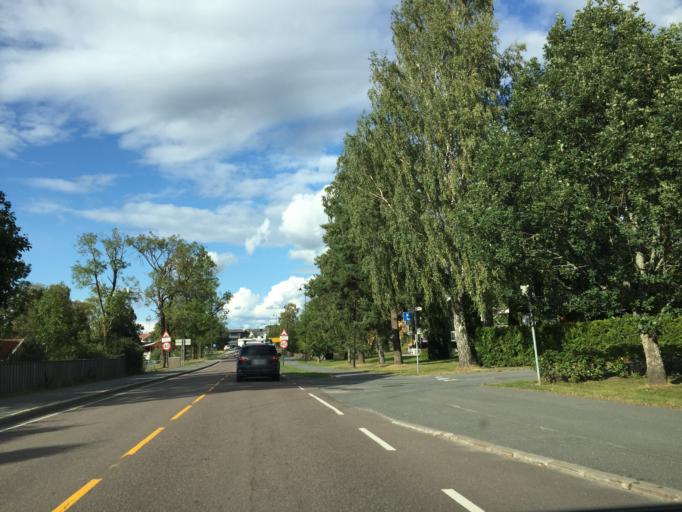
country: NO
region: Ostfold
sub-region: Trogstad
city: Skjonhaug
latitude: 59.6381
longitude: 11.3144
